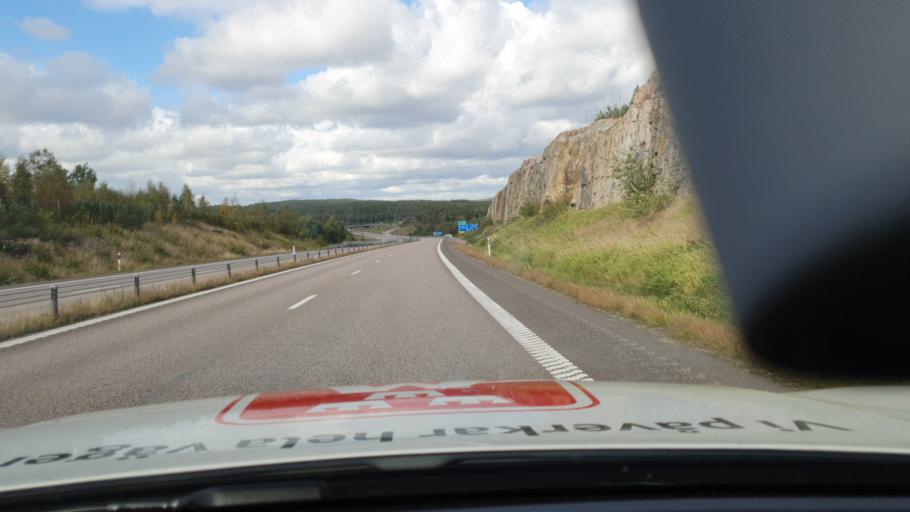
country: SE
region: Vaestra Goetaland
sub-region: Stromstads Kommun
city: Stroemstad
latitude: 58.8682
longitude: 11.2740
